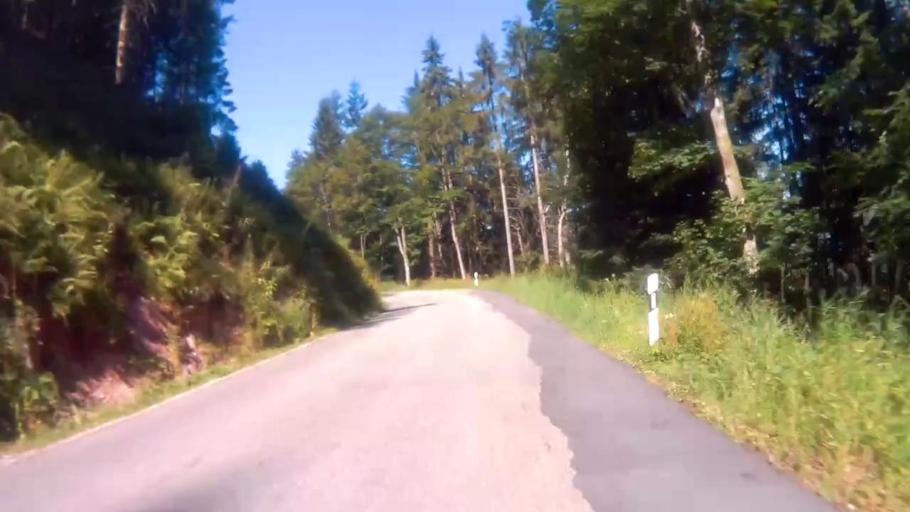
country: DE
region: Baden-Wuerttemberg
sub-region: Freiburg Region
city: Badenweiler
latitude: 47.7858
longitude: 7.7192
